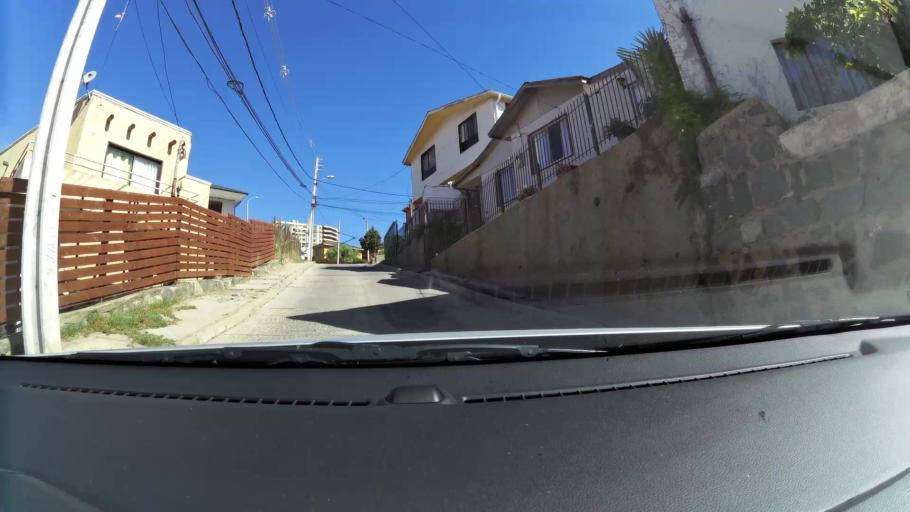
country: CL
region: Valparaiso
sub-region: Provincia de Valparaiso
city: Vina del Mar
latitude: -33.0339
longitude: -71.5721
